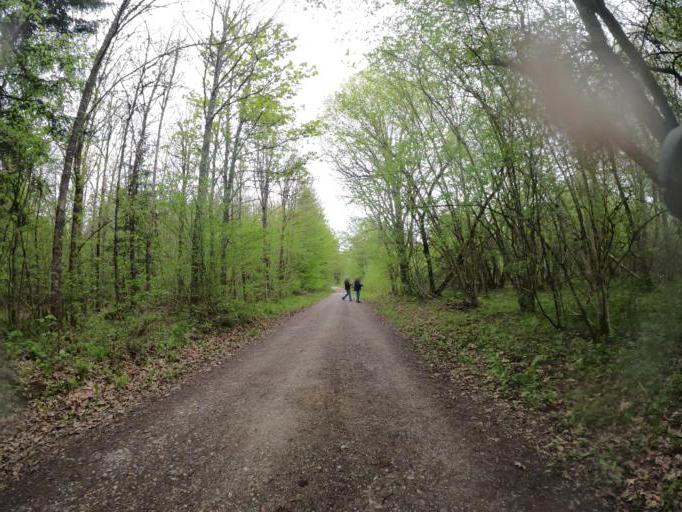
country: DE
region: Baden-Wuerttemberg
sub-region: Regierungsbezirk Stuttgart
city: Motzingen
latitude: 48.5512
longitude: 8.7653
